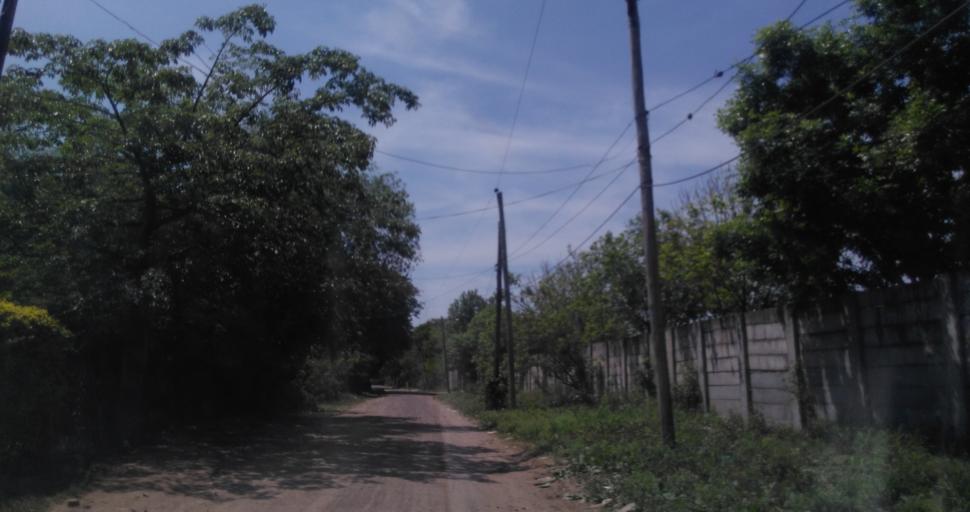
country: AR
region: Chaco
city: Fontana
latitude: -27.4216
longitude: -59.0127
